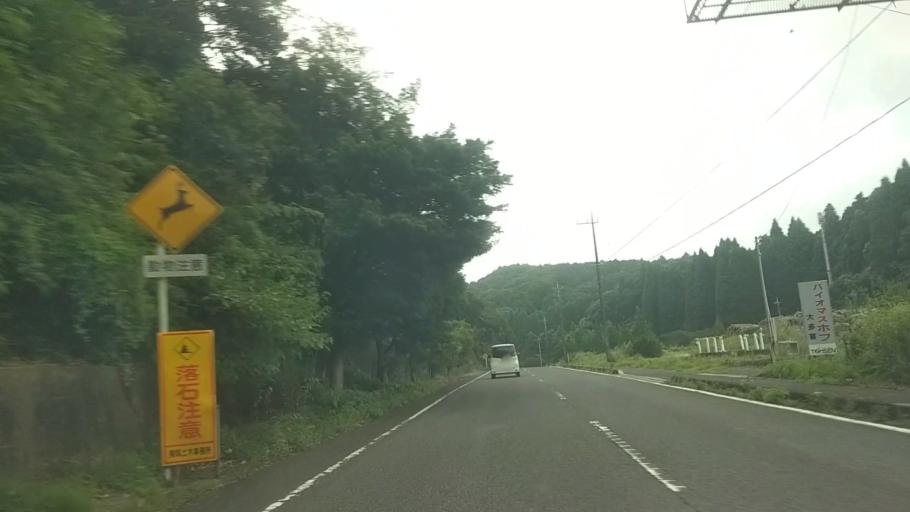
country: JP
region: Chiba
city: Kawaguchi
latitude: 35.2444
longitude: 140.1797
